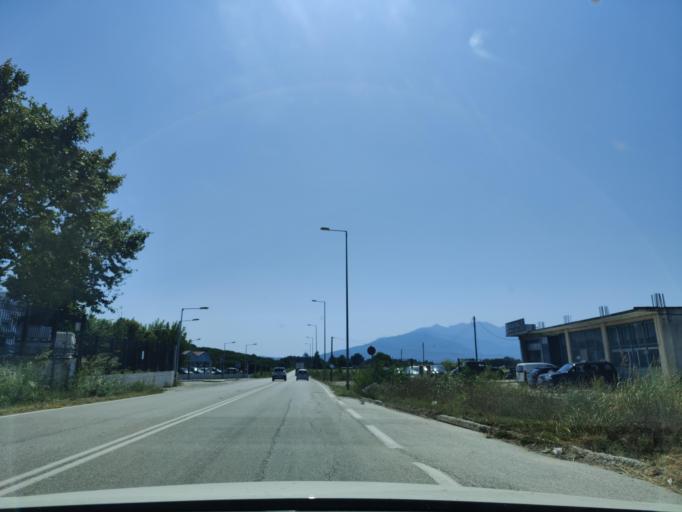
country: GR
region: East Macedonia and Thrace
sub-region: Nomos Kavalas
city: Amygdaleonas
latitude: 40.9757
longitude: 24.3614
